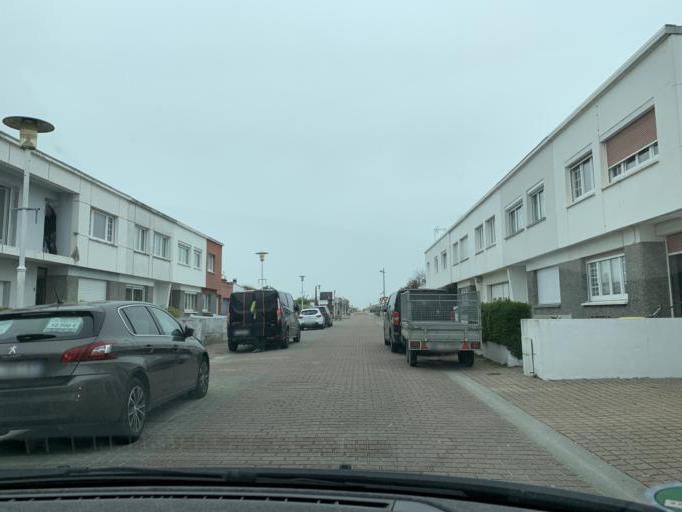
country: FR
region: Nord-Pas-de-Calais
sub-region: Departement du Pas-de-Calais
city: Calais
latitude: 50.9591
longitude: 1.8252
